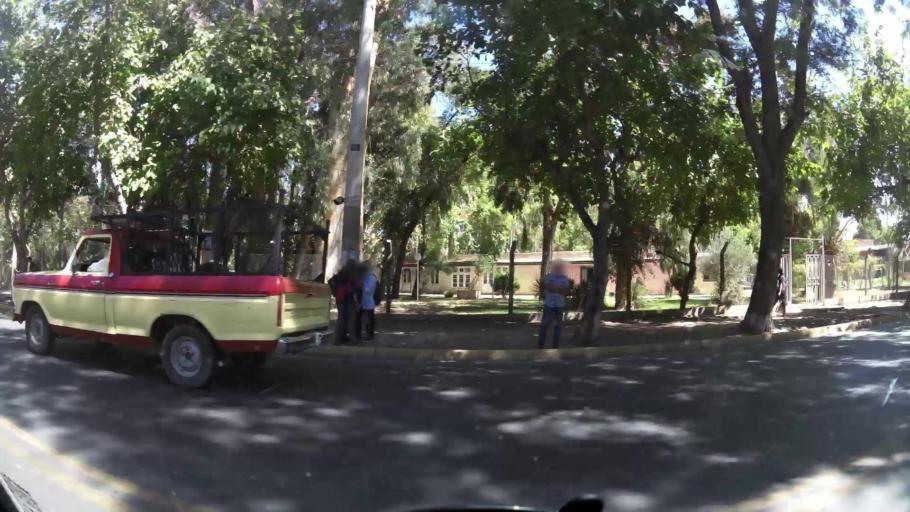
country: AR
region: San Juan
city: San Juan
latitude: -31.5281
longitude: -68.5546
